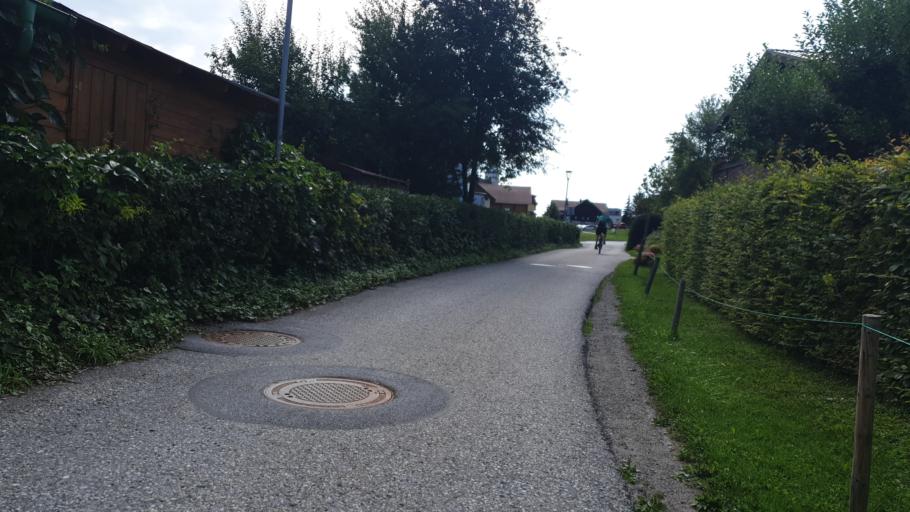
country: AT
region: Salzburg
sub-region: Politischer Bezirk Salzburg-Umgebung
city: Eugendorf
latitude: 47.8681
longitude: 13.1270
